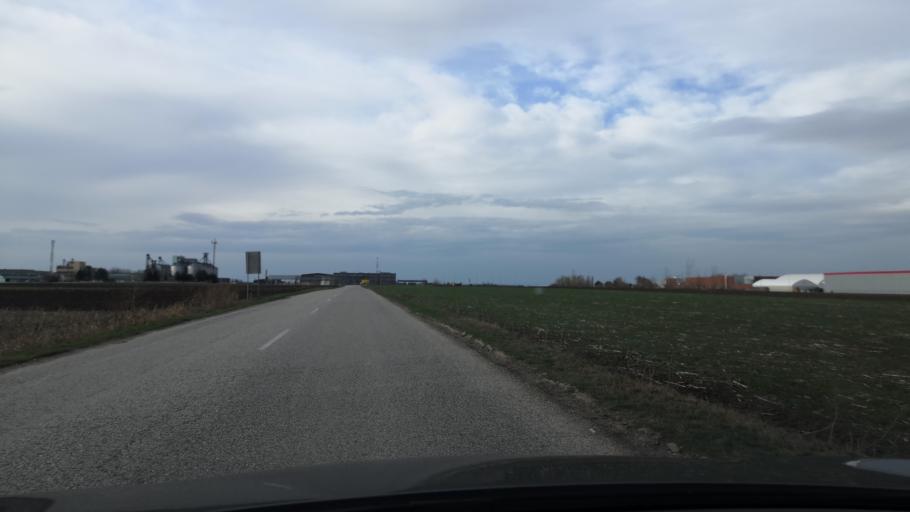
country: RS
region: Autonomna Pokrajina Vojvodina
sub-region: Sremski Okrug
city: Ingija
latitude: 45.0507
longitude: 20.1067
